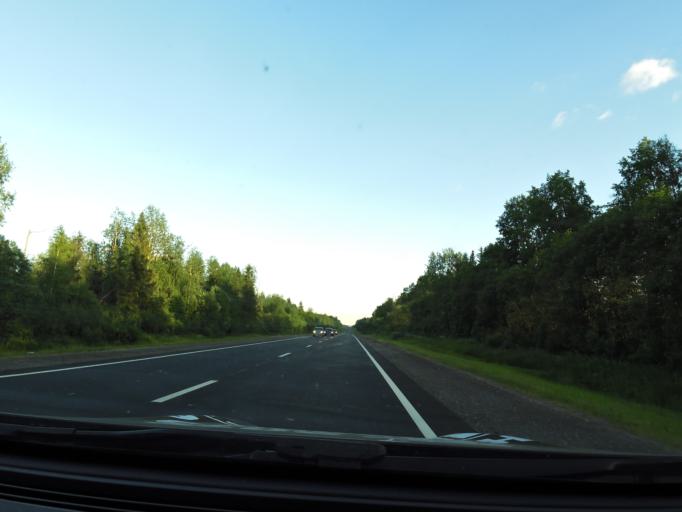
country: RU
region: Vologda
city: Gryazovets
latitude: 58.9081
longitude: 40.1804
